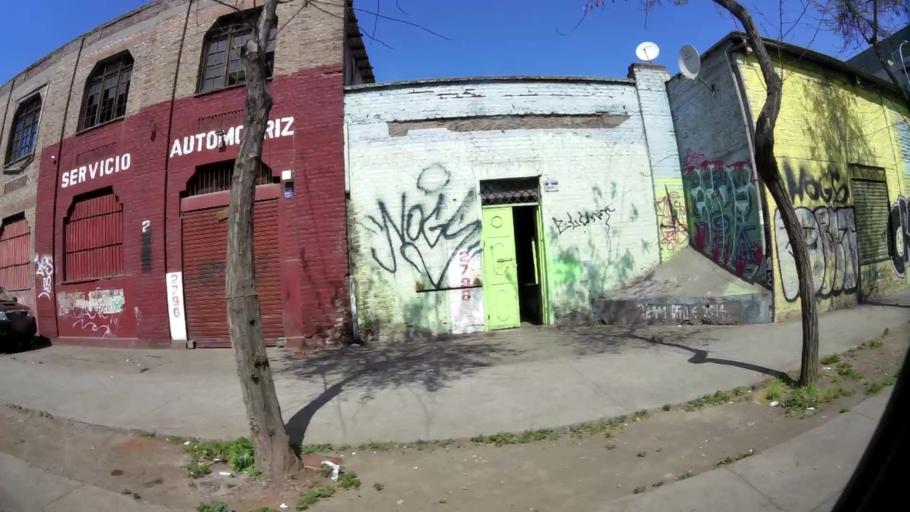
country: CL
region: Santiago Metropolitan
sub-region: Provincia de Santiago
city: Santiago
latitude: -33.4548
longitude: -70.6741
